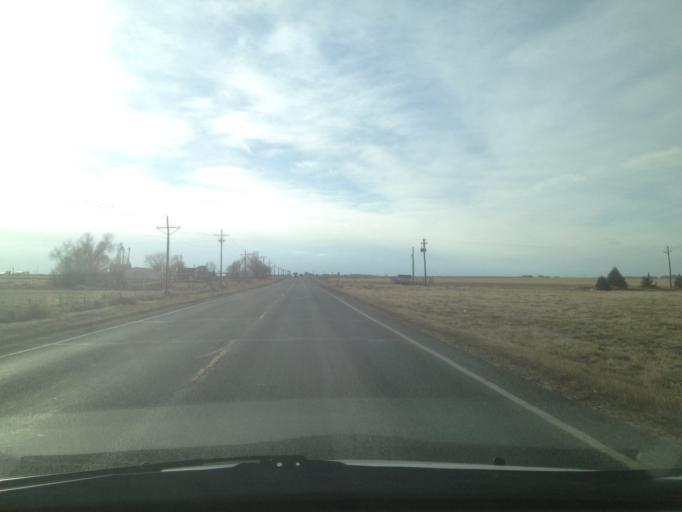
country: US
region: Colorado
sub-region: Weld County
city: Hudson
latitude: 40.0806
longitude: -104.6859
